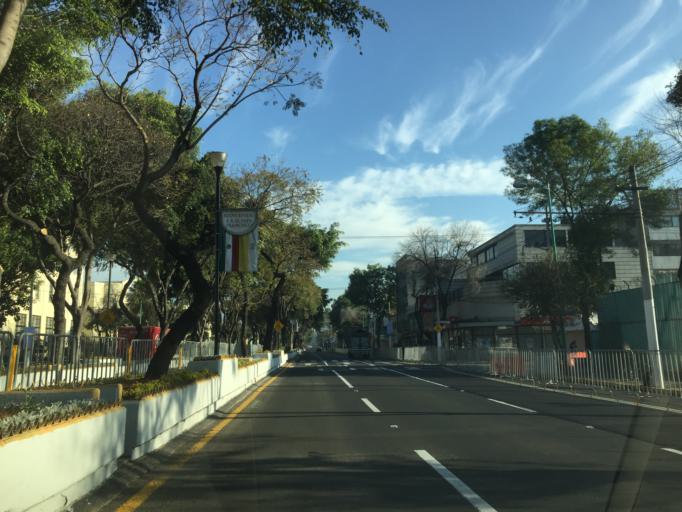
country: MX
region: Mexico
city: Colonia Lindavista
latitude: 19.4745
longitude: -99.1211
